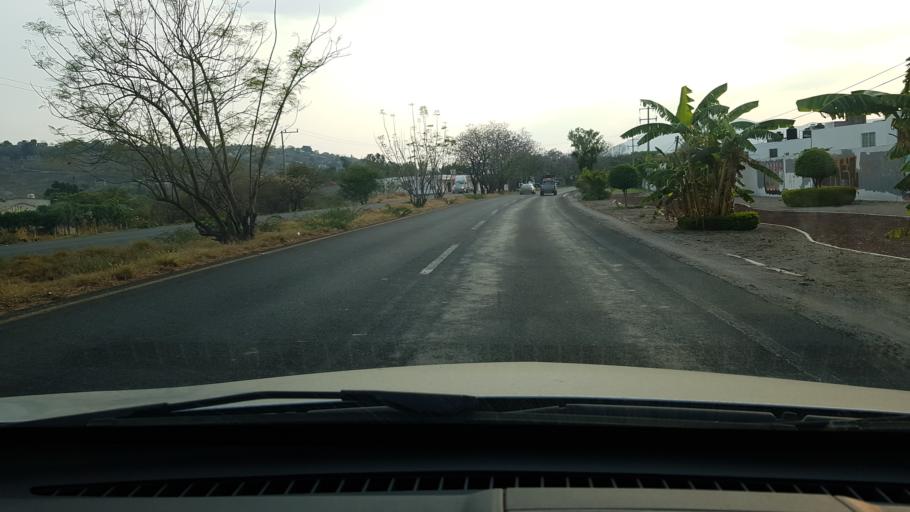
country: MX
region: Morelos
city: Yautepec
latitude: 18.8716
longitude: -99.0606
